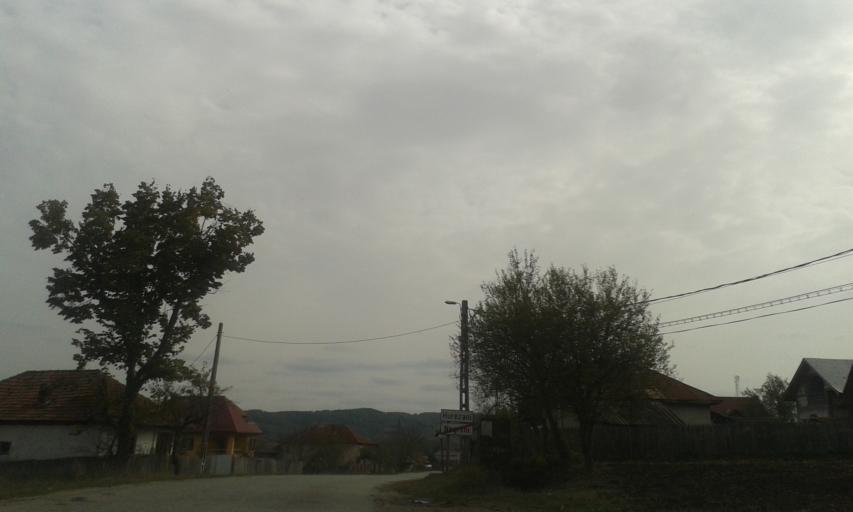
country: RO
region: Gorj
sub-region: Comuna Hurezani
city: Hurezani
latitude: 44.8235
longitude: 23.6481
